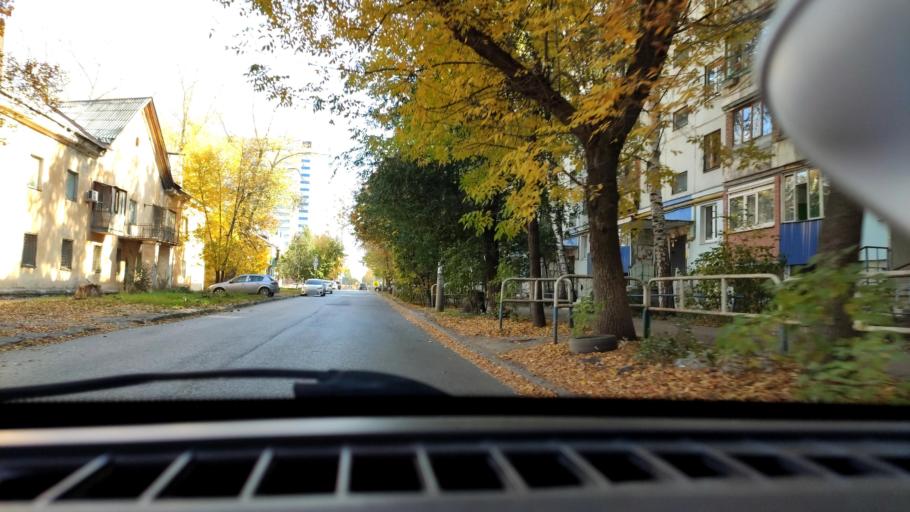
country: RU
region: Samara
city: Samara
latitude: 53.2035
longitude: 50.1753
